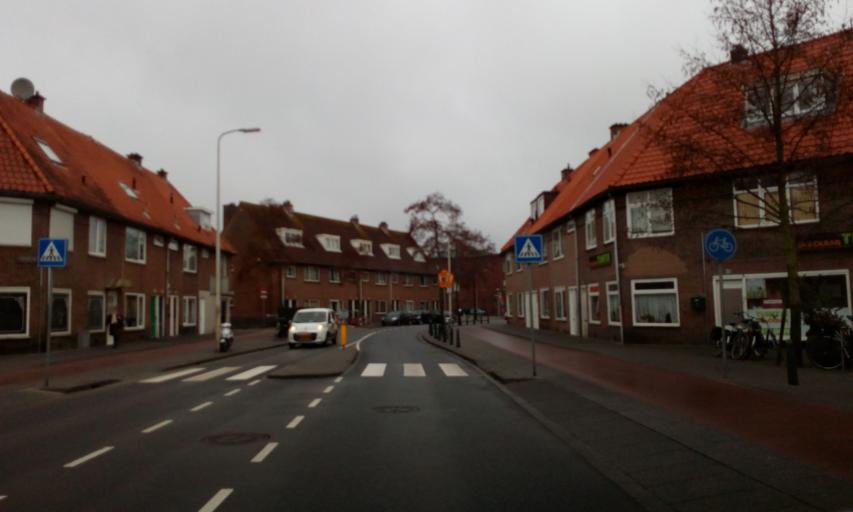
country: NL
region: South Holland
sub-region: Gemeente Rijswijk
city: Rijswijk
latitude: 52.0505
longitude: 4.3138
